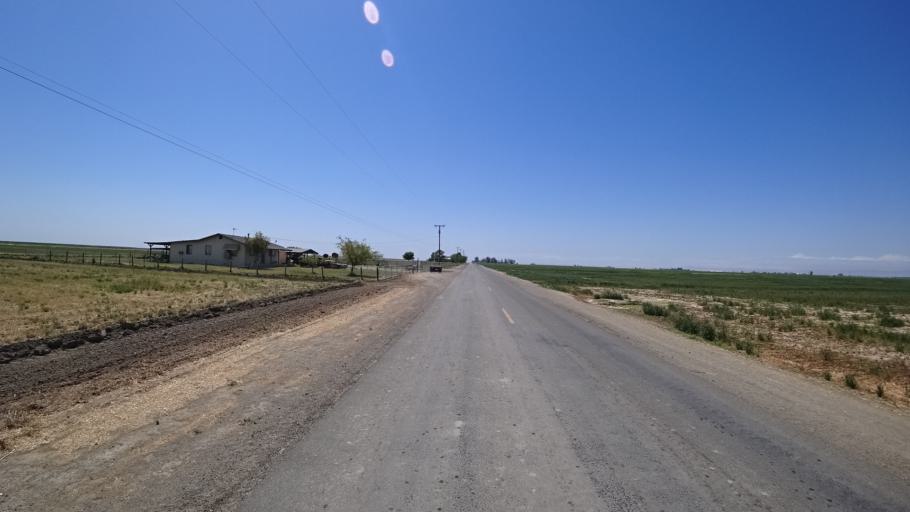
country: US
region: California
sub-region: Kings County
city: Stratford
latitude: 36.2024
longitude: -119.7623
